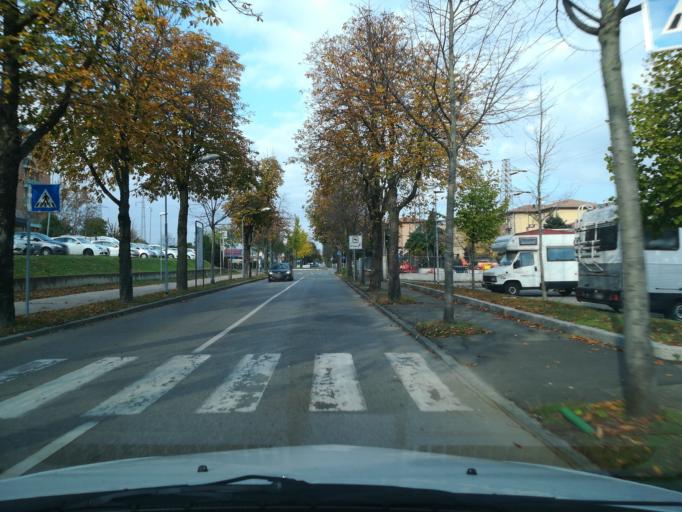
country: IT
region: Emilia-Romagna
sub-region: Provincia di Bologna
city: Imola
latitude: 44.3617
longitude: 11.7218
